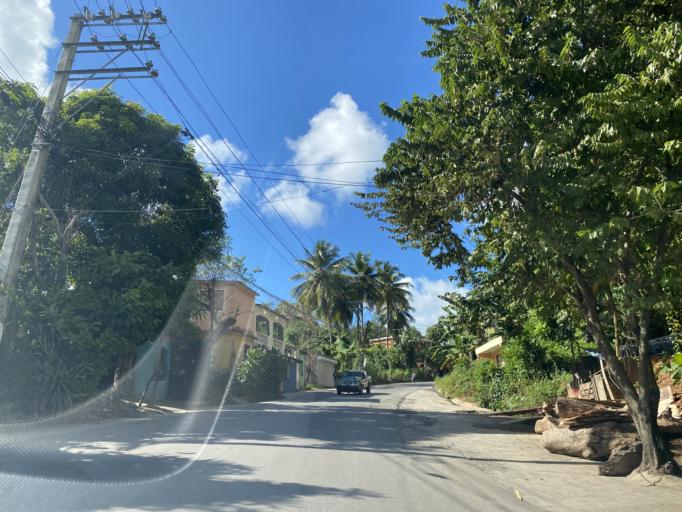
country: DO
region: Samana
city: Samana
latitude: 19.2079
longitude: -69.3540
